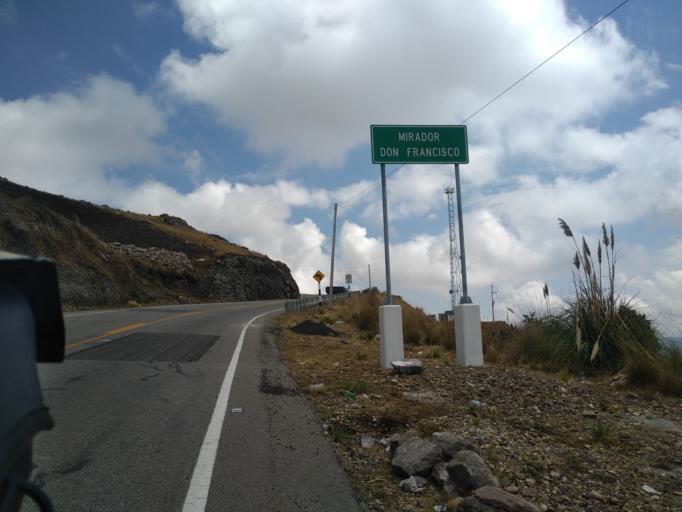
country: PE
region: La Libertad
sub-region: Provincia de Santiago de Chuco
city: Quiruvilca
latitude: -7.9179
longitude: -78.1587
